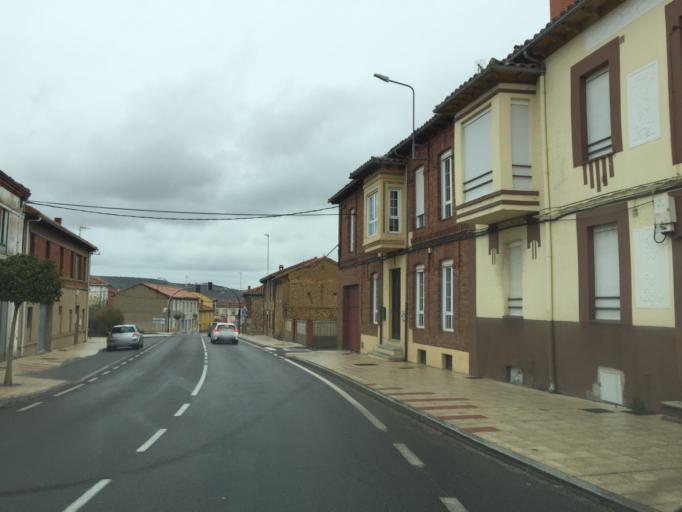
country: ES
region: Castille and Leon
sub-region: Provincia de Leon
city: Sariegos
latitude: 42.6692
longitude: -5.6336
